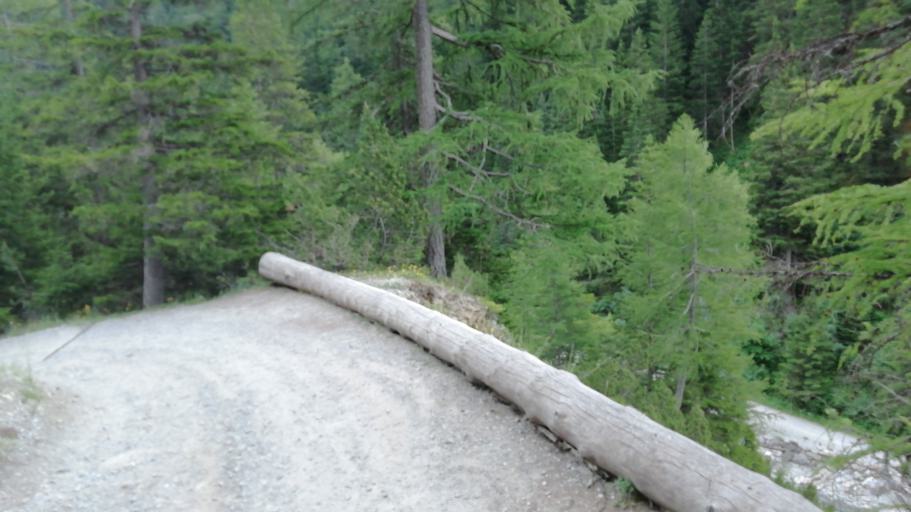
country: IT
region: Lombardy
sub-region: Provincia di Sondrio
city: Sant'Antonio
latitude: 46.4780
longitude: 10.4559
